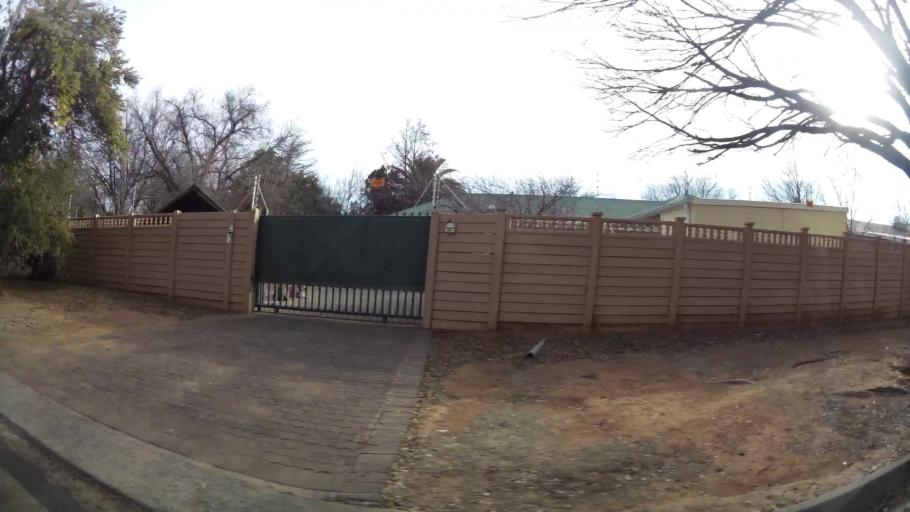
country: ZA
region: Orange Free State
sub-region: Mangaung Metropolitan Municipality
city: Bloemfontein
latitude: -29.1225
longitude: 26.1777
